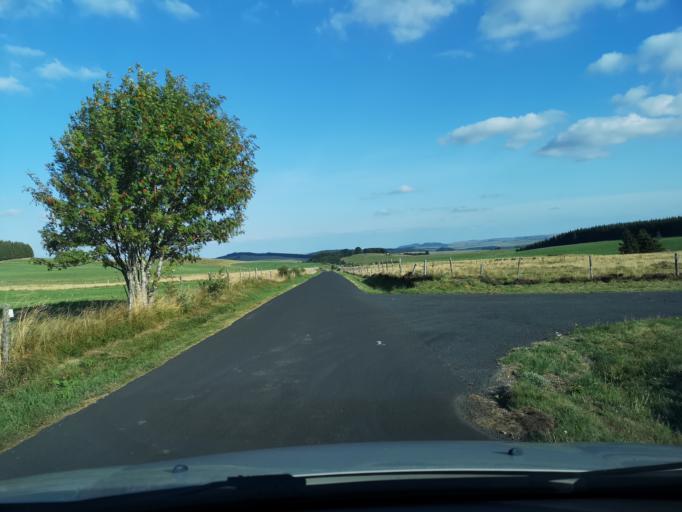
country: FR
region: Auvergne
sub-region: Departement du Puy-de-Dome
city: Mont-Dore
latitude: 45.4896
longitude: 2.8950
